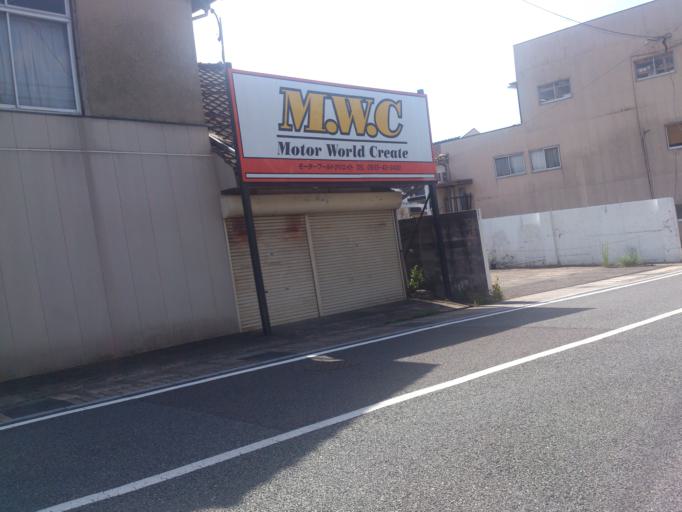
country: JP
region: Saga Prefecture
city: Imaricho-ko
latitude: 33.1828
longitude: 129.8806
